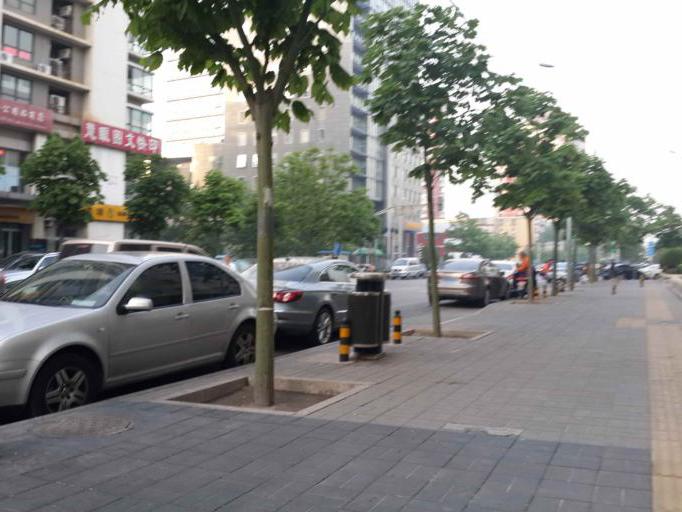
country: CN
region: Beijing
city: Chaowai
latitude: 39.9256
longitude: 116.4336
